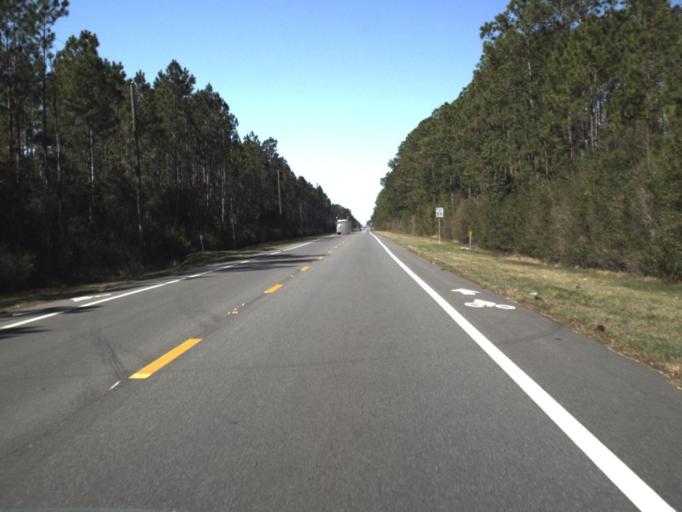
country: US
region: Florida
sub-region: Bay County
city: Callaway
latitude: 30.1528
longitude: -85.5329
